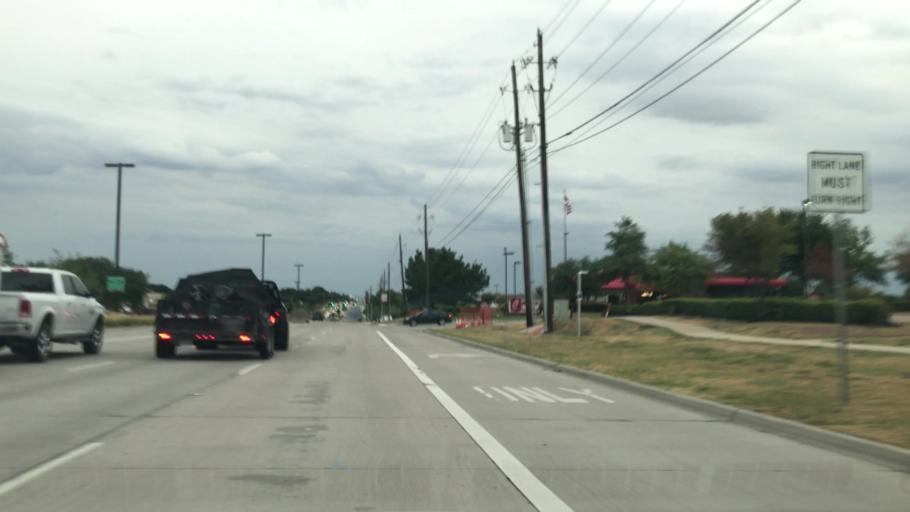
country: US
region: Texas
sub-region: Dallas County
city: Carrollton
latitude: 32.9852
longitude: -96.9097
